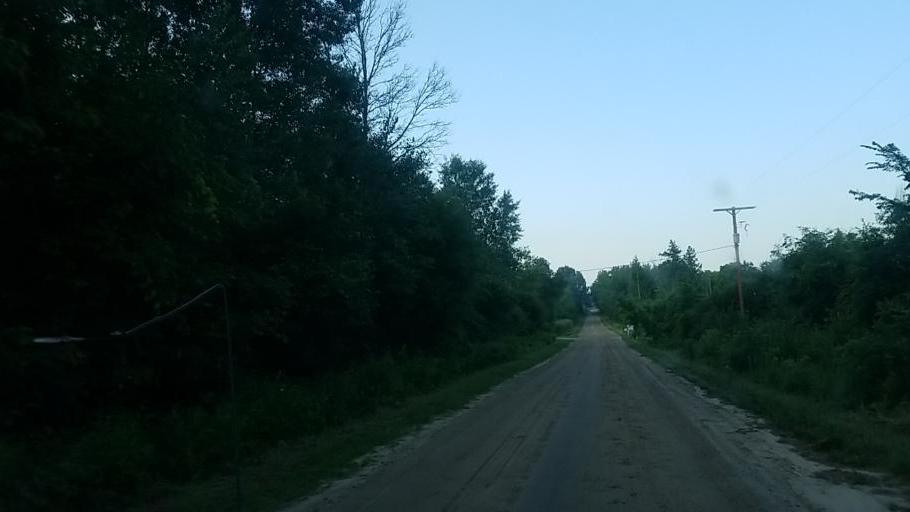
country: US
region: Michigan
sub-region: Osceola County
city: Evart
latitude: 43.9086
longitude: -85.1679
